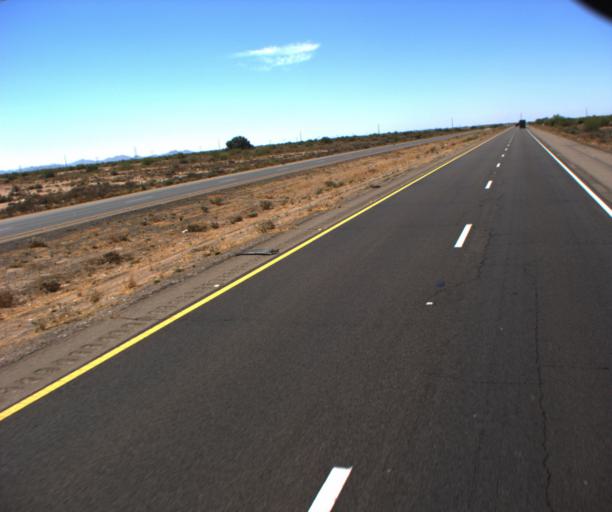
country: US
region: Arizona
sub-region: Pinal County
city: Maricopa
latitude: 33.1594
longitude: -112.0081
